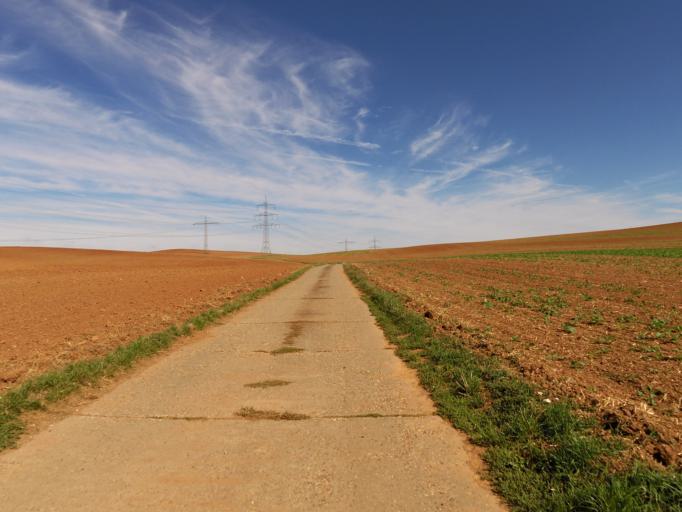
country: DE
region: Rheinland-Pfalz
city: Borrstadt
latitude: 49.5812
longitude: 7.9567
